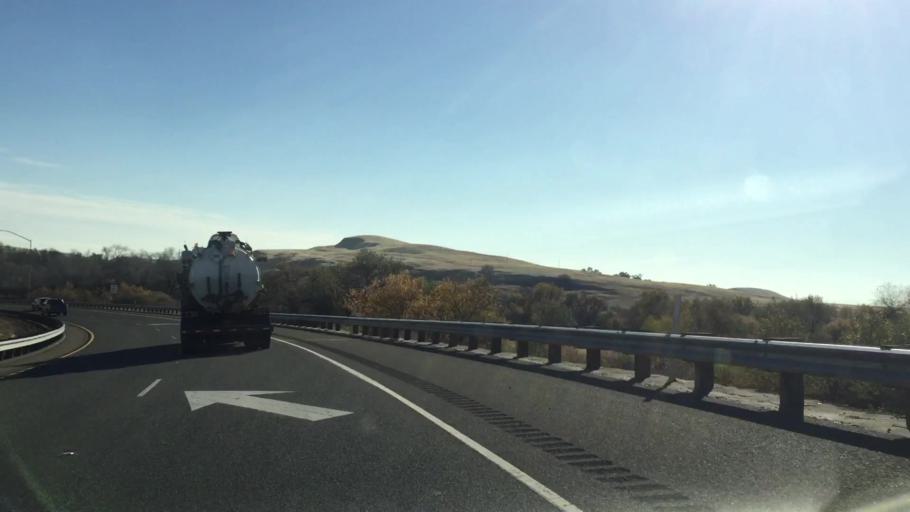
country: US
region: California
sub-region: Butte County
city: Thermalito
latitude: 39.5812
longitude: -121.6225
